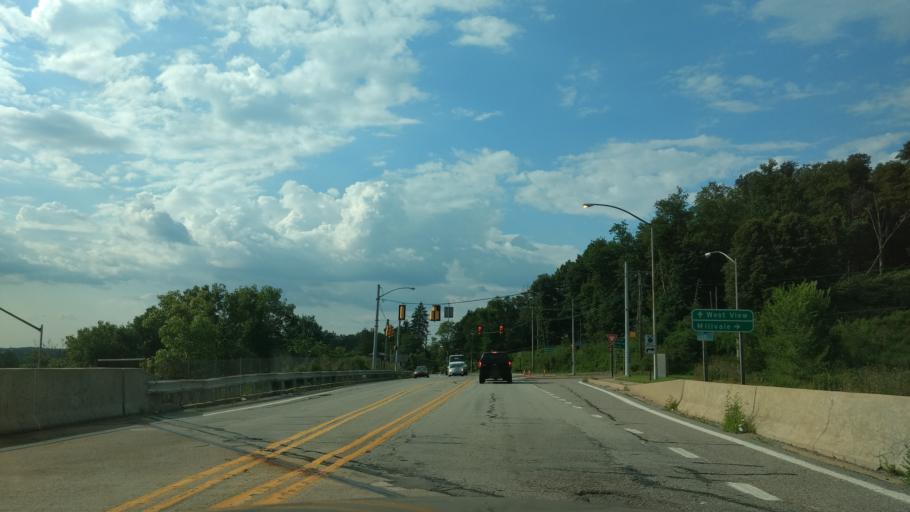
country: US
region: Pennsylvania
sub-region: Allegheny County
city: West View
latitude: 40.4976
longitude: -80.0200
